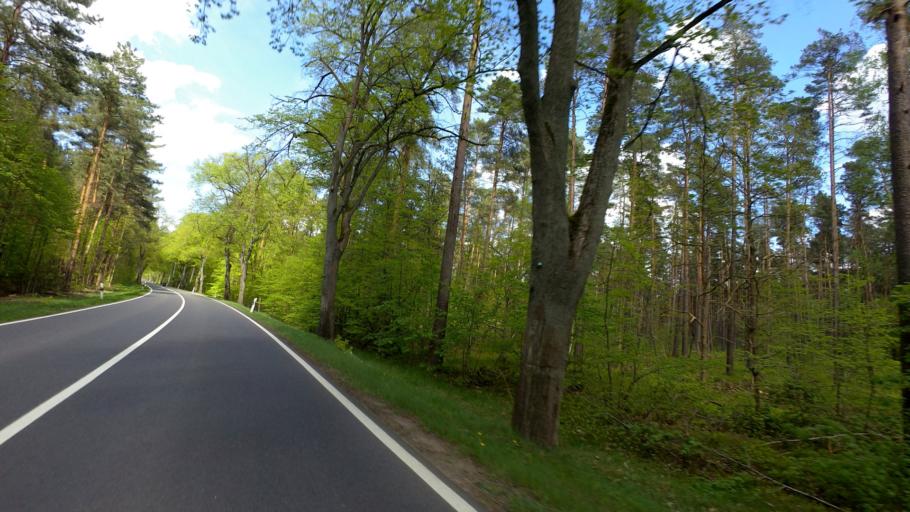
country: DE
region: Brandenburg
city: Friedrichswalde
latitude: 53.0079
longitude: 13.6005
